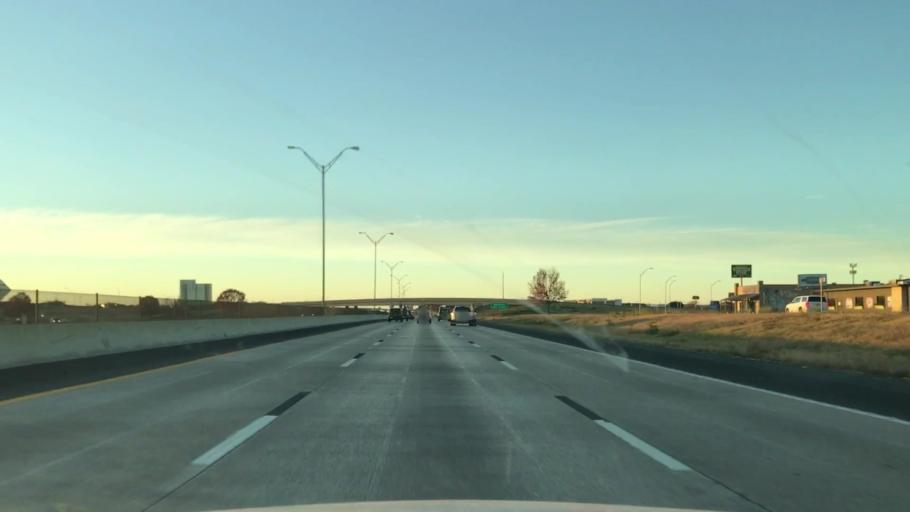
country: US
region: Texas
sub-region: Johnson County
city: Burleson
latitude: 32.5816
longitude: -97.3197
